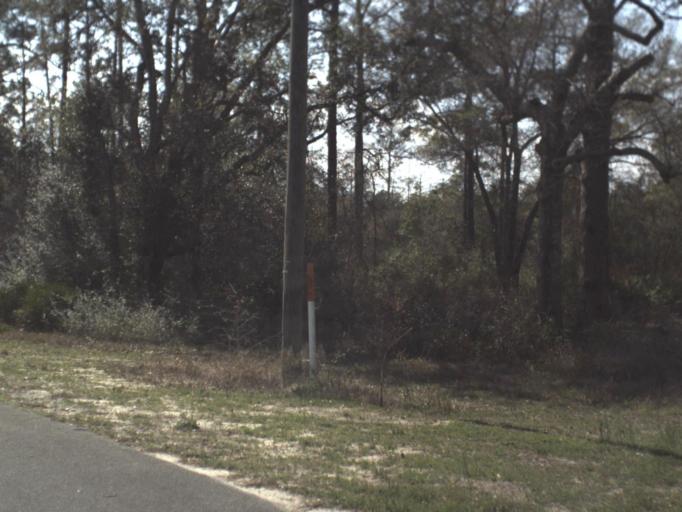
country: US
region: Florida
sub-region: Wakulla County
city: Crawfordville
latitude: 30.0710
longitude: -84.4483
